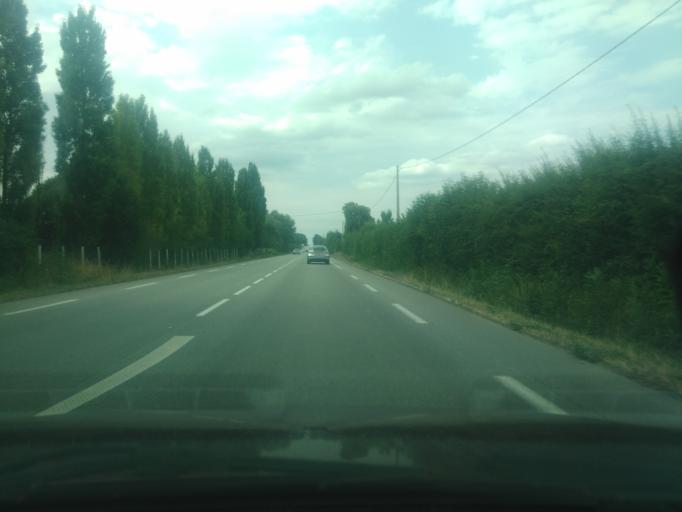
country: FR
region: Pays de la Loire
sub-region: Departement de la Vendee
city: Sainte-Cecile
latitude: 46.7241
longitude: -1.0751
